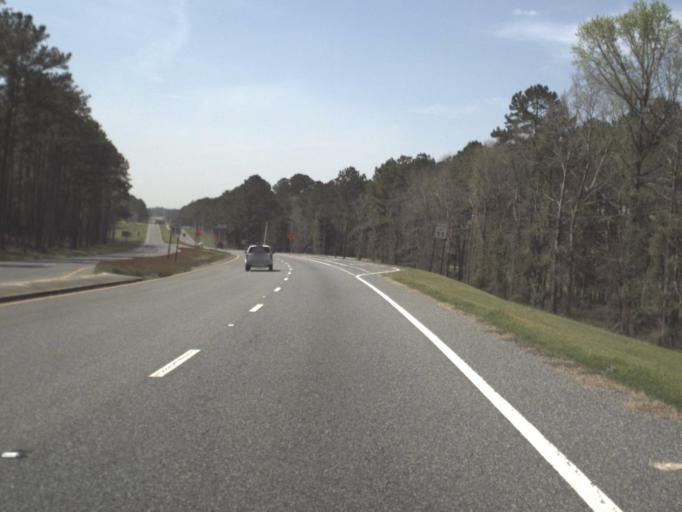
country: US
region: Florida
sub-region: Gadsden County
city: Midway
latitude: 30.5518
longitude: -84.4918
